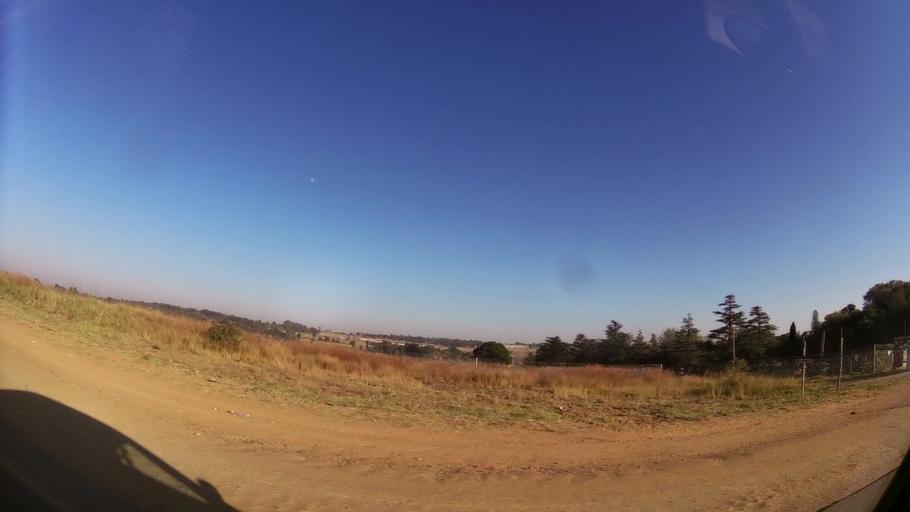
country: ZA
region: Gauteng
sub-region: City of Johannesburg Metropolitan Municipality
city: Midrand
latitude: -25.9328
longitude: 28.0968
